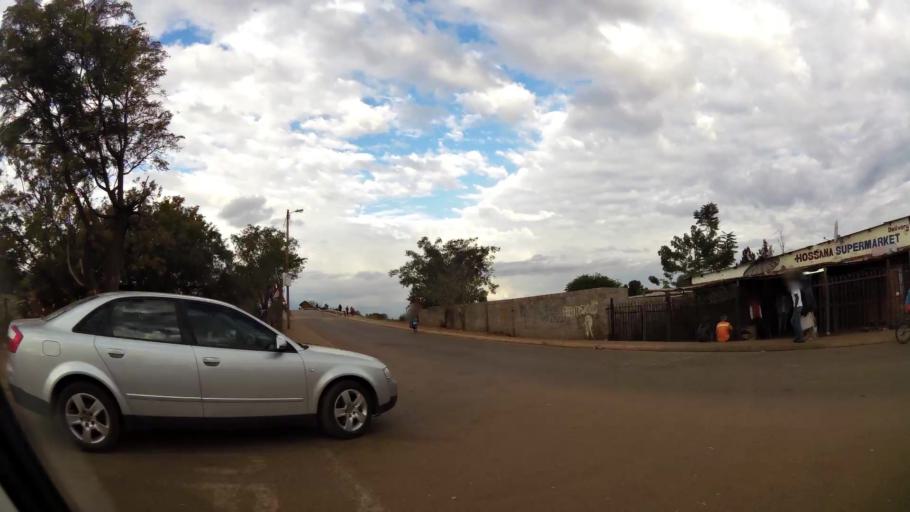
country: ZA
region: Limpopo
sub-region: Waterberg District Municipality
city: Modimolle
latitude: -24.5214
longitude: 28.7257
